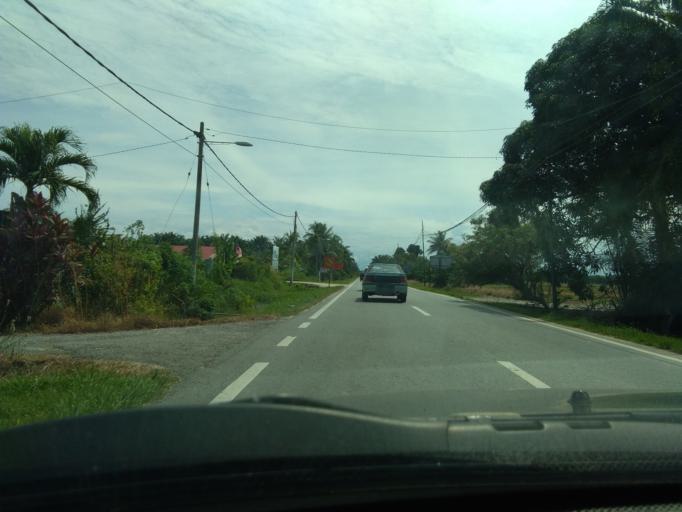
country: MY
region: Perak
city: Bagan Serai
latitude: 5.0395
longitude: 100.5722
